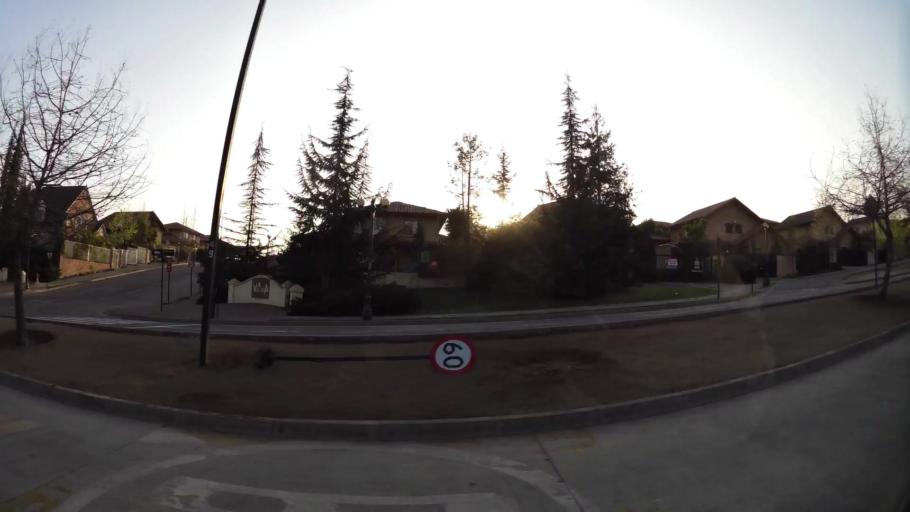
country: CL
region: Santiago Metropolitan
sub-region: Provincia de Santiago
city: Villa Presidente Frei, Nunoa, Santiago, Chile
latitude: -33.3304
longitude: -70.5113
